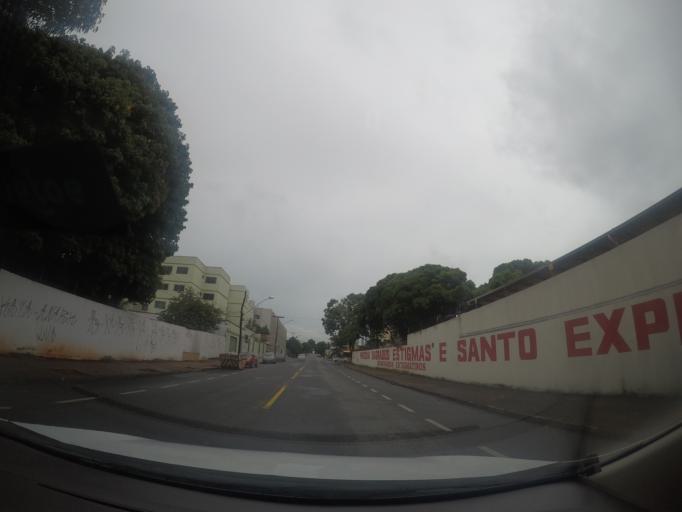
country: BR
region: Goias
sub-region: Goiania
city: Goiania
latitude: -16.7113
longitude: -49.2835
